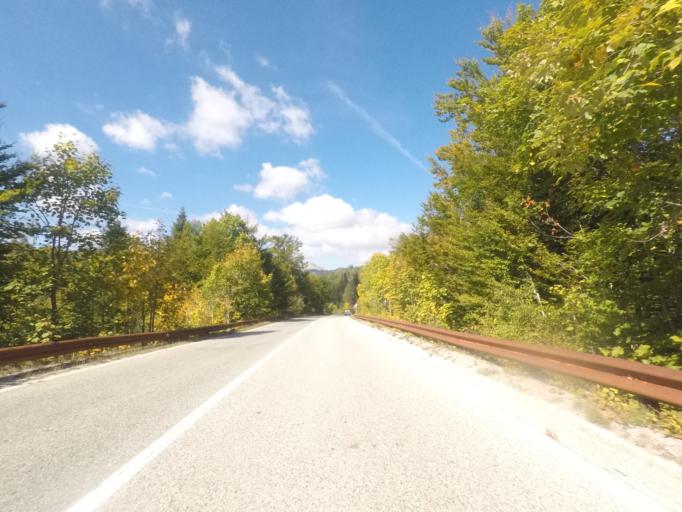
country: ME
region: Opstina Pluzine
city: Pluzine
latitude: 42.9775
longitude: 18.9002
